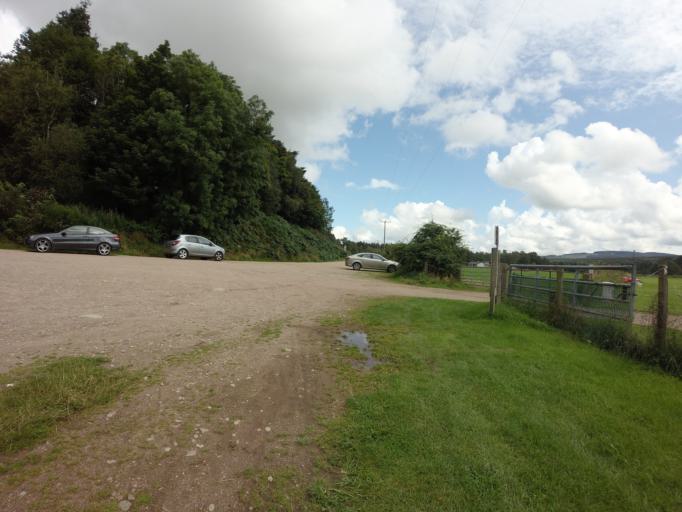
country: GB
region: Scotland
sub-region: Aberdeenshire
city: Banchory
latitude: 57.0564
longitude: -2.4246
